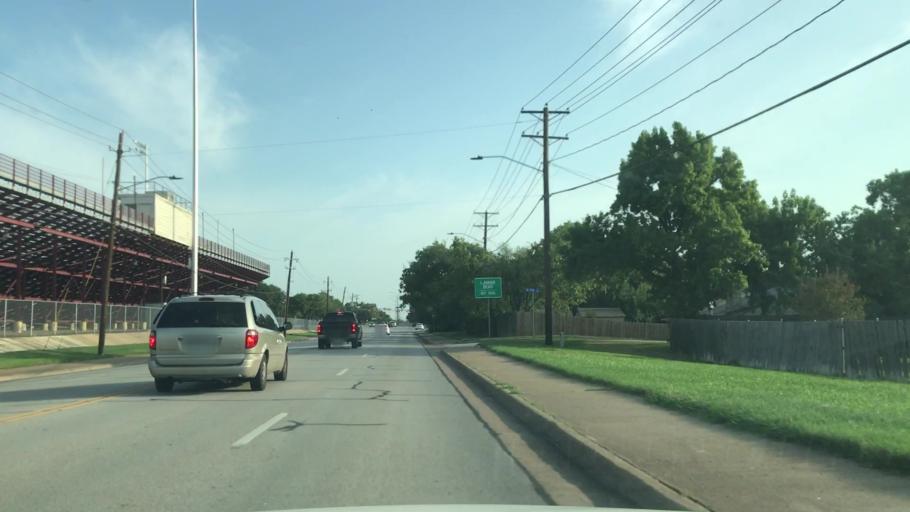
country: US
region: Texas
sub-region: Tarrant County
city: Arlington
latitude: 32.7621
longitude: -97.1230
